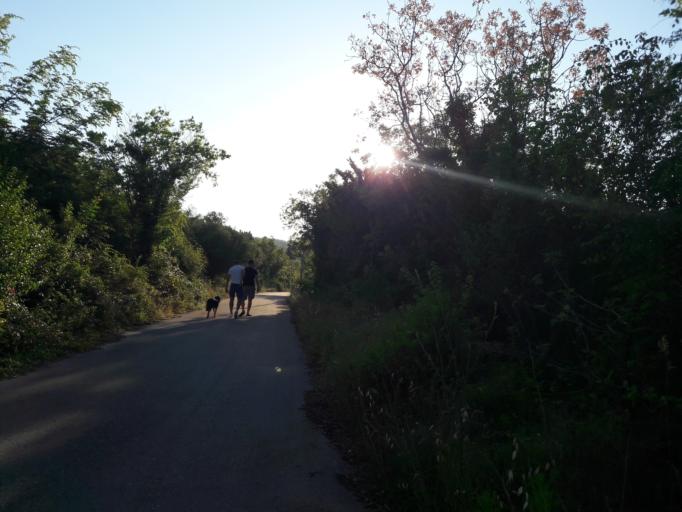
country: HR
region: Sibensko-Kniniska
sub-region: Grad Sibenik
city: Sibenik
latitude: 43.6929
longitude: 15.8441
